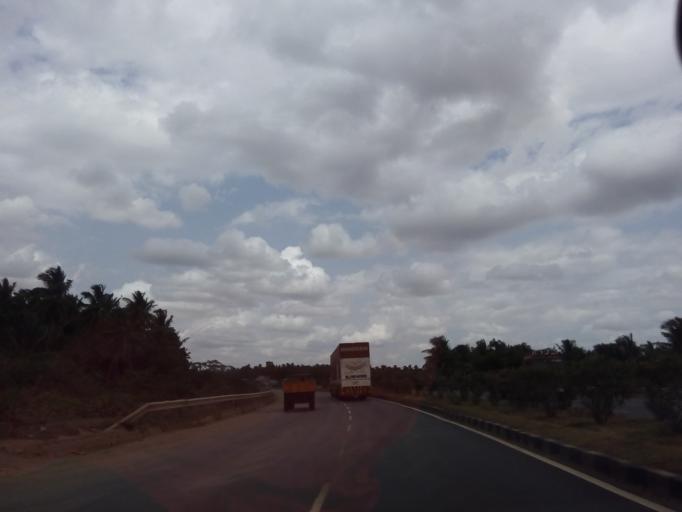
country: IN
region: Karnataka
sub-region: Chitradurga
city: Hiriyur
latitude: 13.9271
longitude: 76.6324
